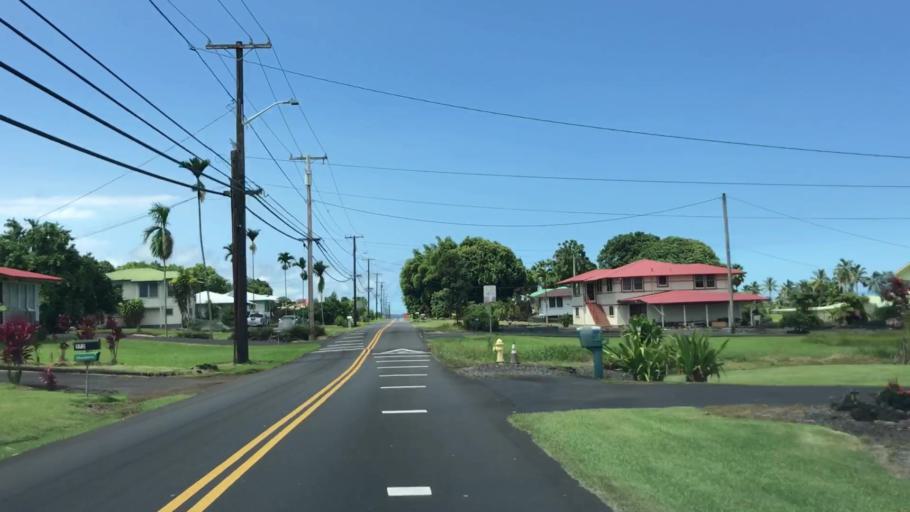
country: US
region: Hawaii
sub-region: Hawaii County
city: Hilo
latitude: 19.6783
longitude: -155.0801
